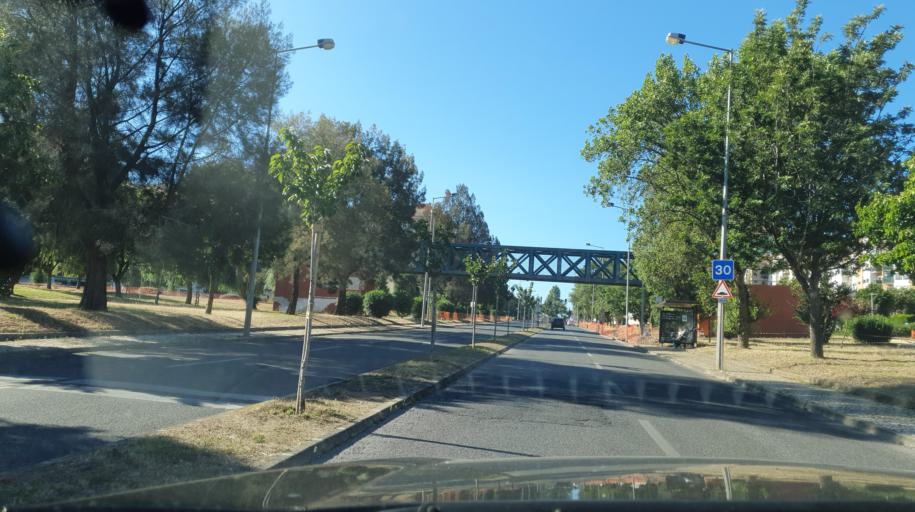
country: PT
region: Lisbon
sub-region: Sintra
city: Cacem
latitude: 38.7621
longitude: -9.2786
